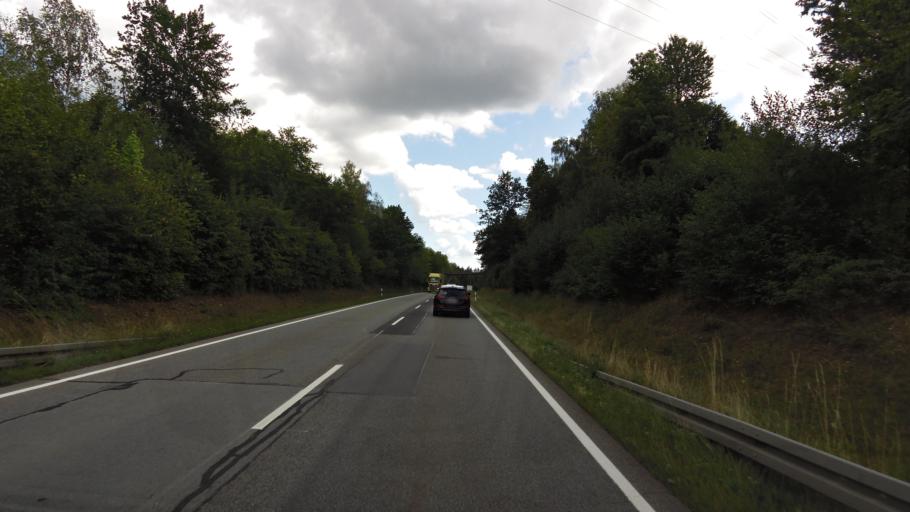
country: DE
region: Bavaria
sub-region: Lower Bavaria
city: Stallwang
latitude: 49.0479
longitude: 12.6482
